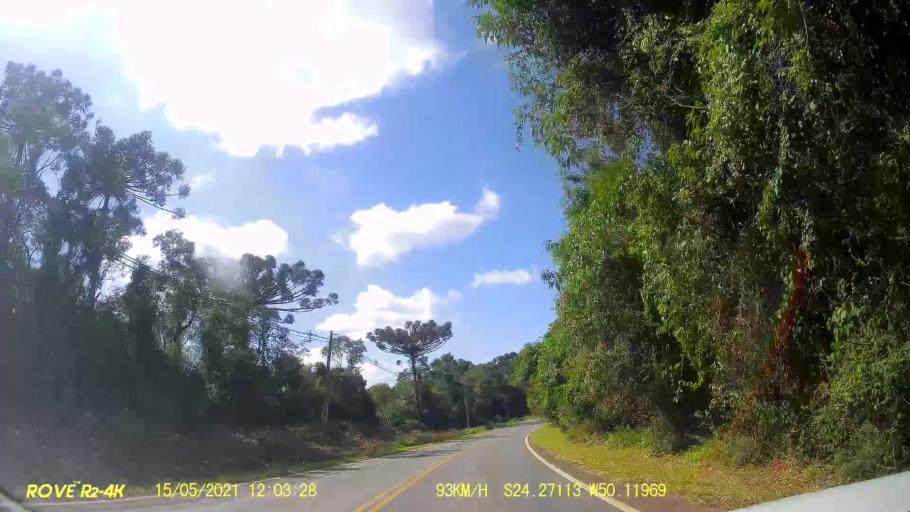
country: BR
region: Parana
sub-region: Pirai Do Sul
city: Pirai do Sul
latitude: -24.2711
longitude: -50.1198
